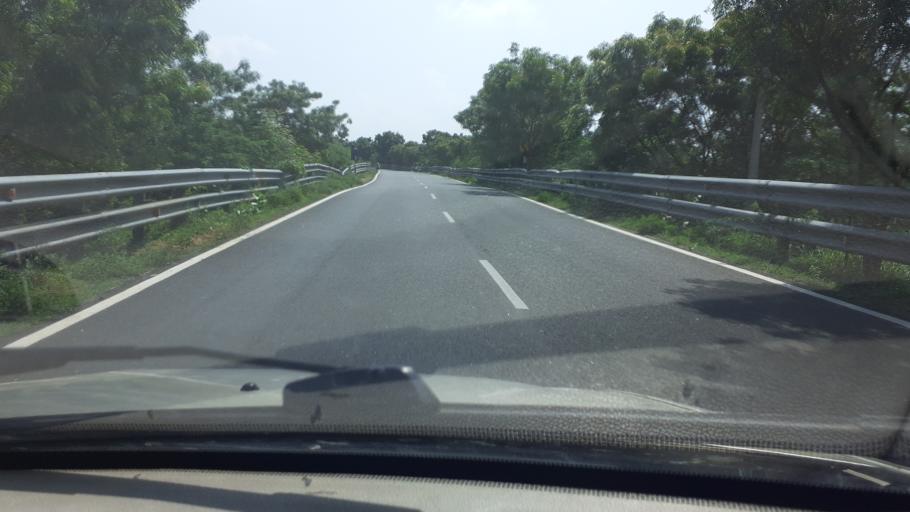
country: IN
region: Tamil Nadu
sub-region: Thoothukkudi
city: Srivaikuntam
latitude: 8.6176
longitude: 77.9136
